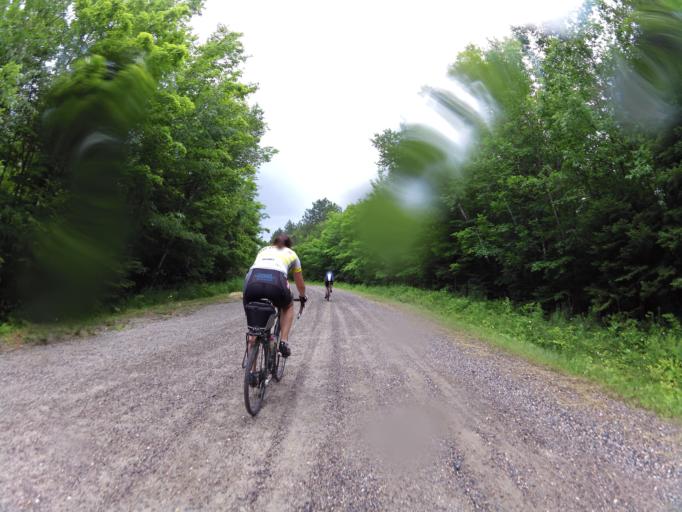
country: CA
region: Ontario
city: Renfrew
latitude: 45.1057
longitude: -76.6136
